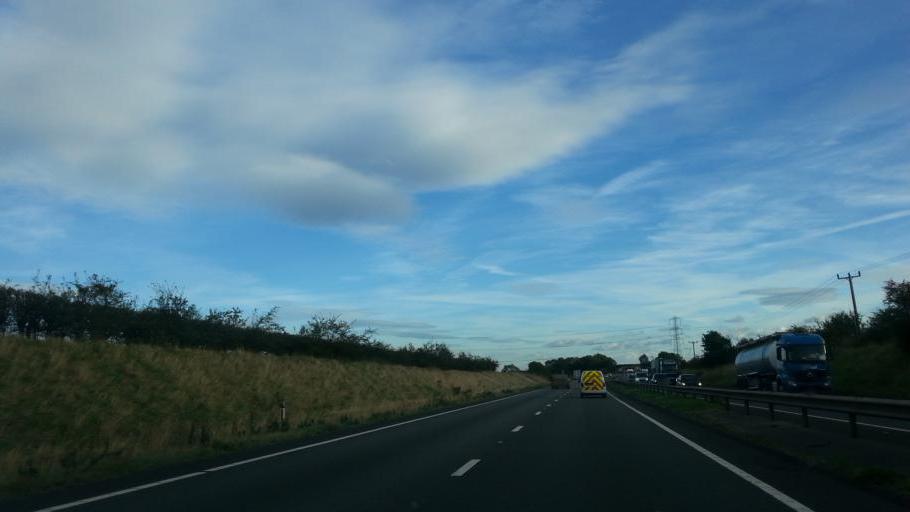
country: GB
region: England
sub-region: Nottinghamshire
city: Tuxford
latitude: 53.1890
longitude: -0.8318
